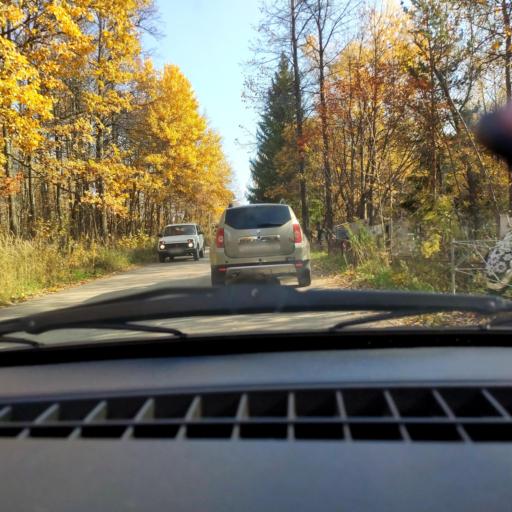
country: RU
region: Bashkortostan
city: Mikhaylovka
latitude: 54.8121
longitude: 55.8651
